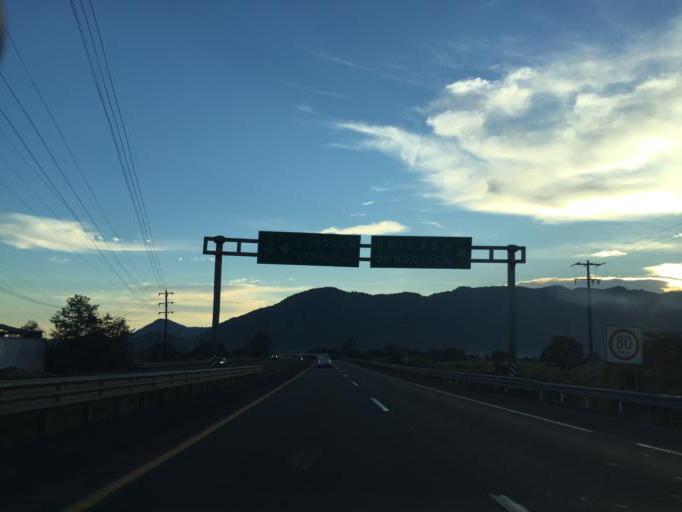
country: MX
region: Veracruz
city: Jalapilla
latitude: 18.8309
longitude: -97.0963
